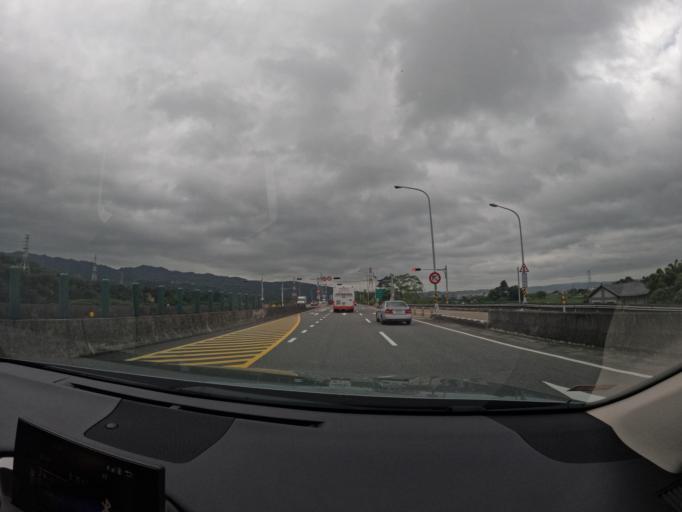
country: TW
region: Taiwan
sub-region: Miaoli
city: Miaoli
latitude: 24.4662
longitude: 120.8239
